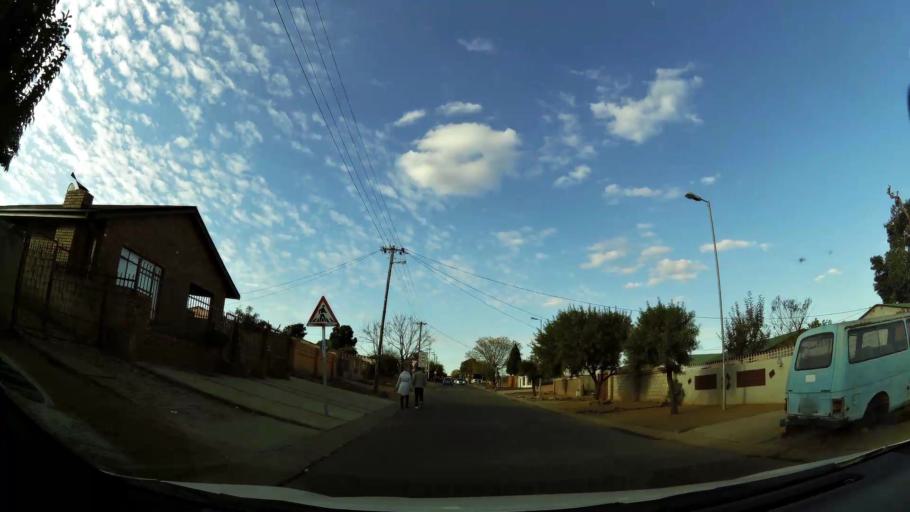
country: ZA
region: Gauteng
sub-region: City of Tshwane Metropolitan Municipality
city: Cullinan
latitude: -25.7060
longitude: 28.3837
